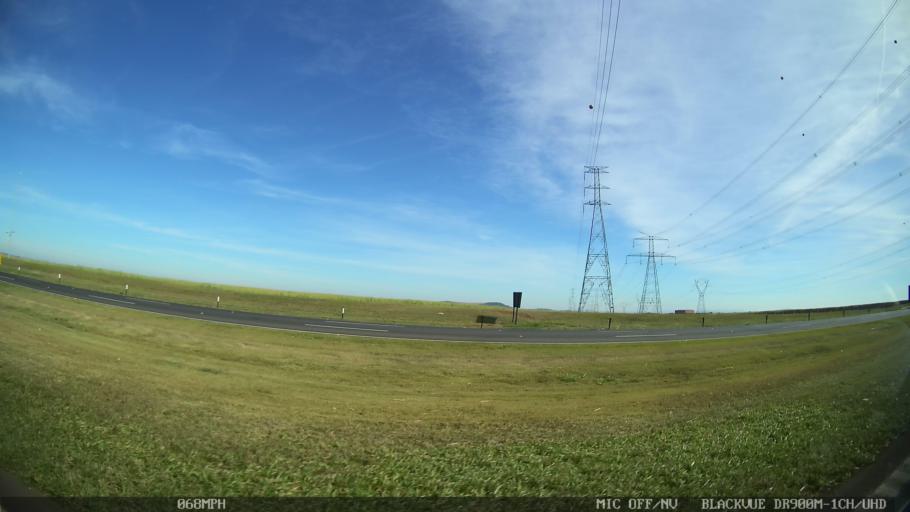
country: BR
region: Sao Paulo
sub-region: Cordeiropolis
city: Cordeiropolis
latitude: -22.4418
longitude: -47.3974
